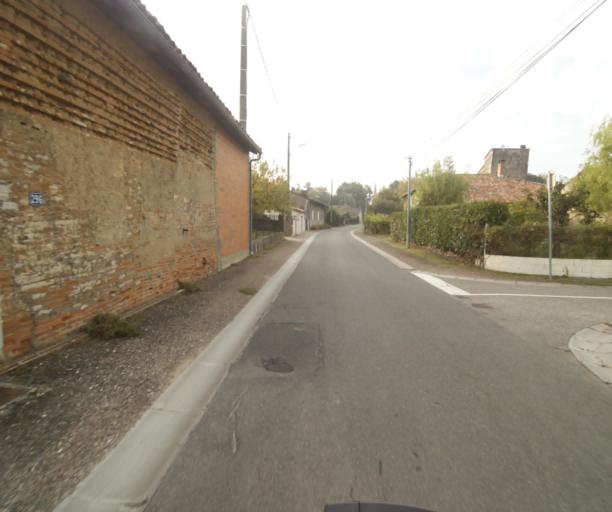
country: FR
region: Midi-Pyrenees
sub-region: Departement du Tarn-et-Garonne
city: Montech
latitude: 43.9612
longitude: 1.2290
